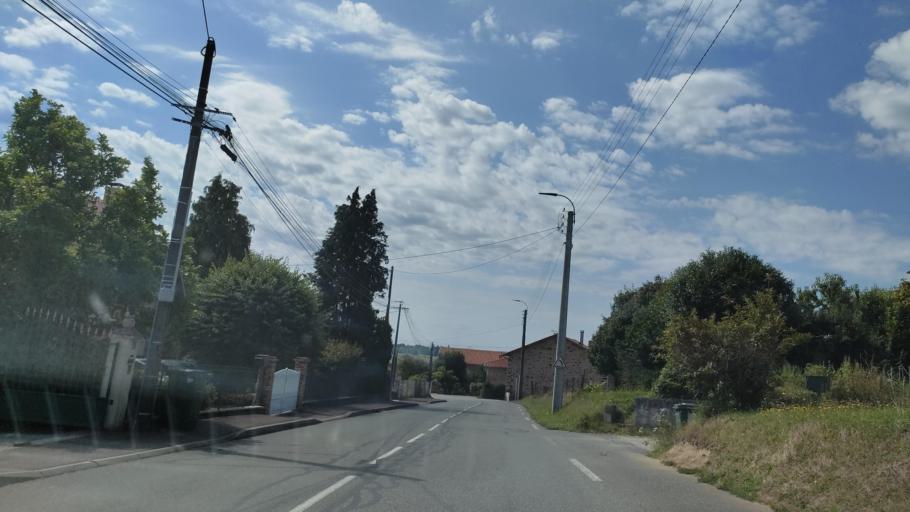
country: FR
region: Limousin
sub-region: Departement de la Haute-Vienne
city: Isle
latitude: 45.8289
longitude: 1.1985
